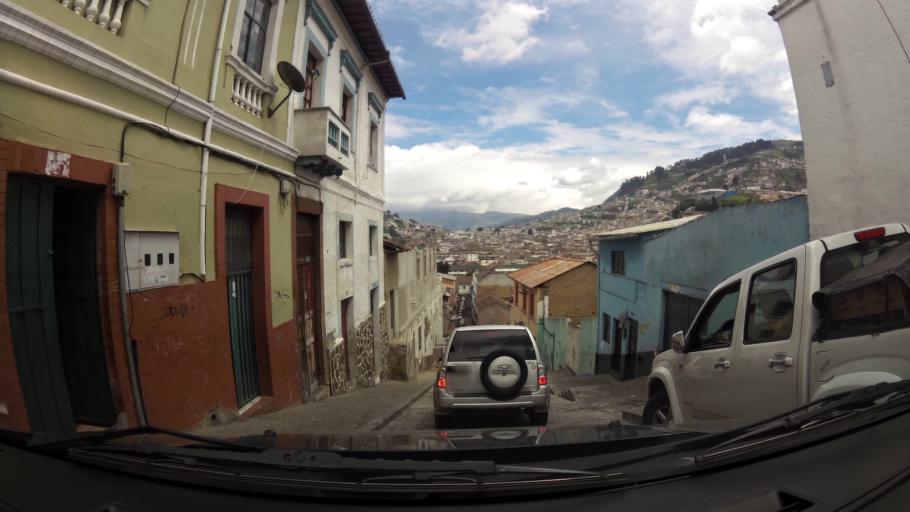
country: EC
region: Pichincha
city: Quito
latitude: -0.2157
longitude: -78.5123
